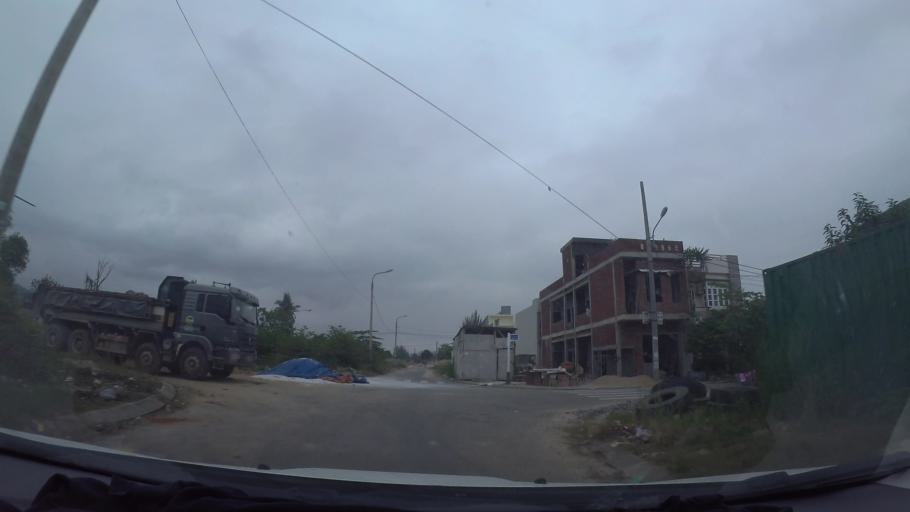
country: VN
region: Da Nang
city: Lien Chieu
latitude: 16.0772
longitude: 108.1567
